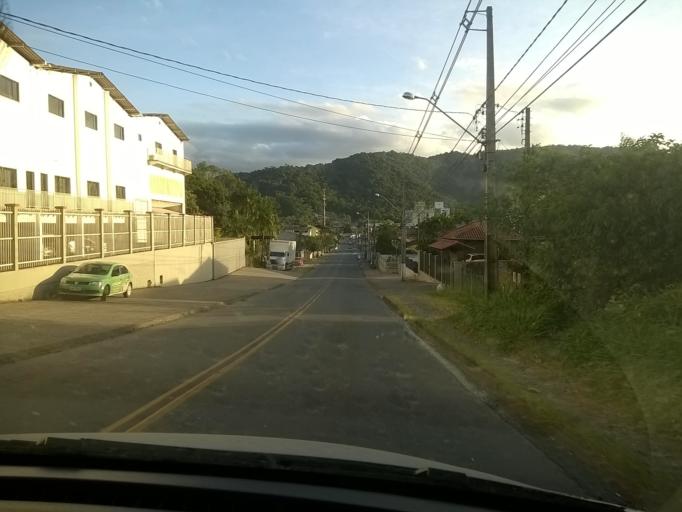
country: BR
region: Santa Catarina
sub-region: Blumenau
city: Blumenau
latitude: -26.9279
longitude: -49.1351
